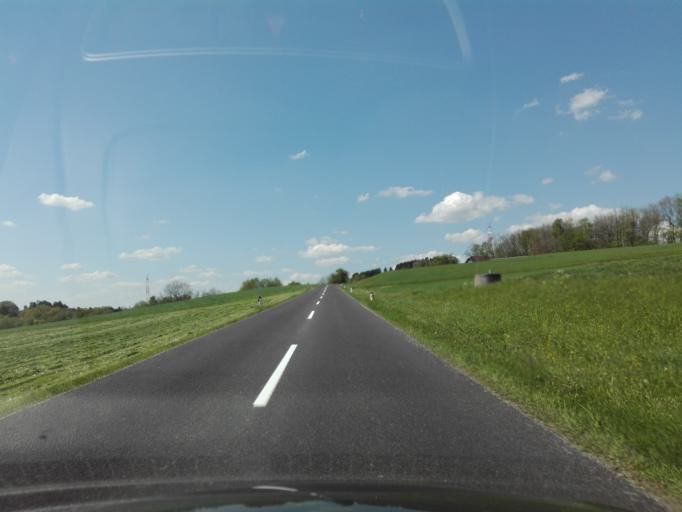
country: AT
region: Upper Austria
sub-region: Politischer Bezirk Rohrbach
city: Kleinzell im Muehlkreis
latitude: 48.3574
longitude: 13.9388
